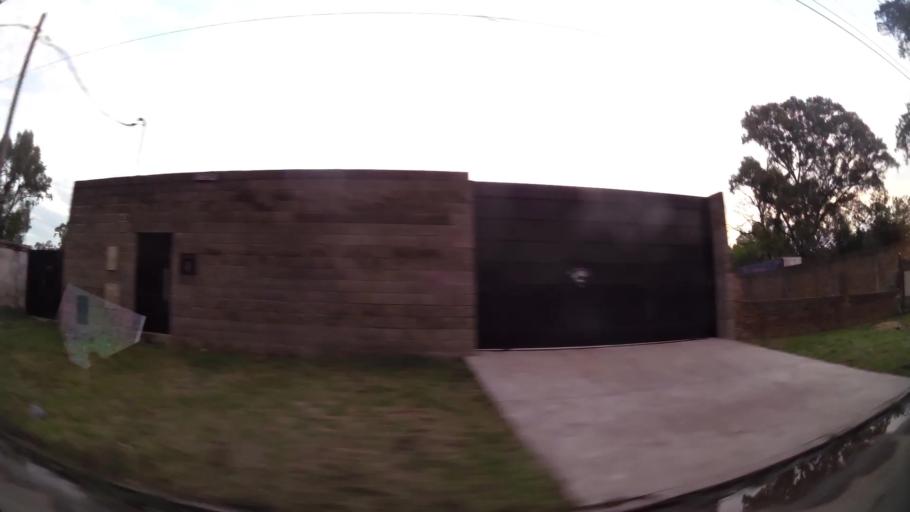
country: AR
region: Buenos Aires
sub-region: Partido de Lomas de Zamora
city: Lomas de Zamora
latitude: -34.7550
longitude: -58.3649
